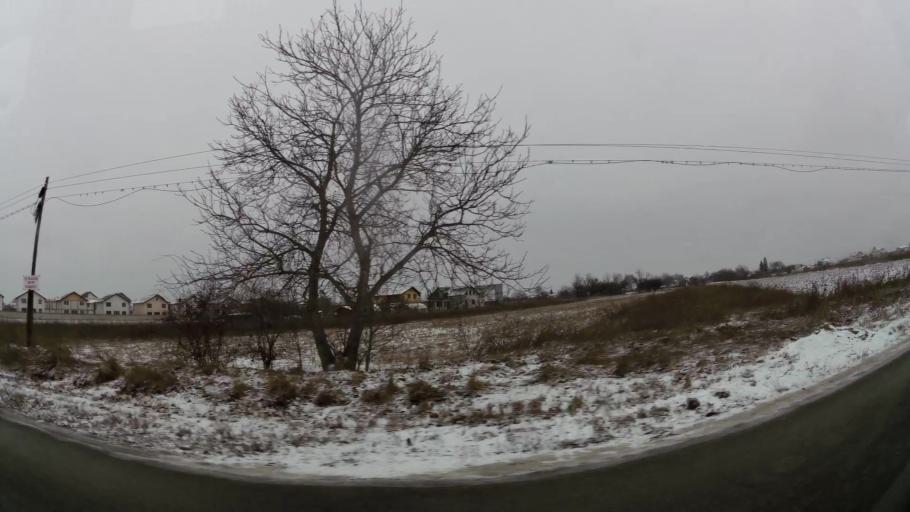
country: RO
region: Dambovita
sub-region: Comuna Ulmi
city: Ulmi
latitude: 44.8911
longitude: 25.5177
